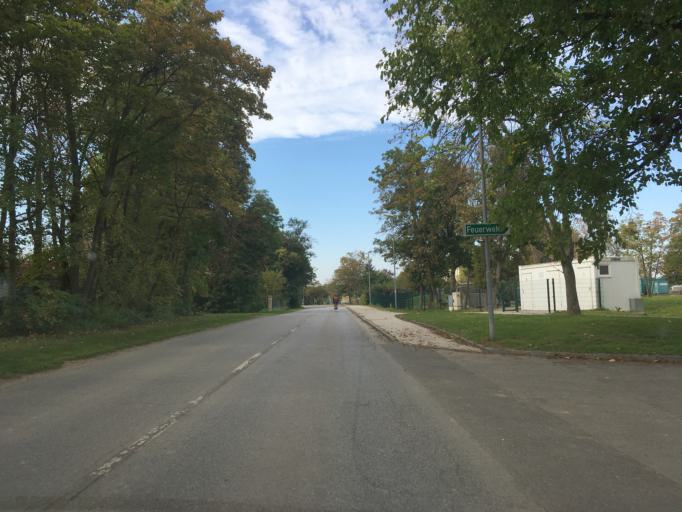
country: AT
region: Lower Austria
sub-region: Politischer Bezirk Bruck an der Leitha
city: Trautmannsdorf an der Leitha
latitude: 48.0231
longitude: 16.6441
